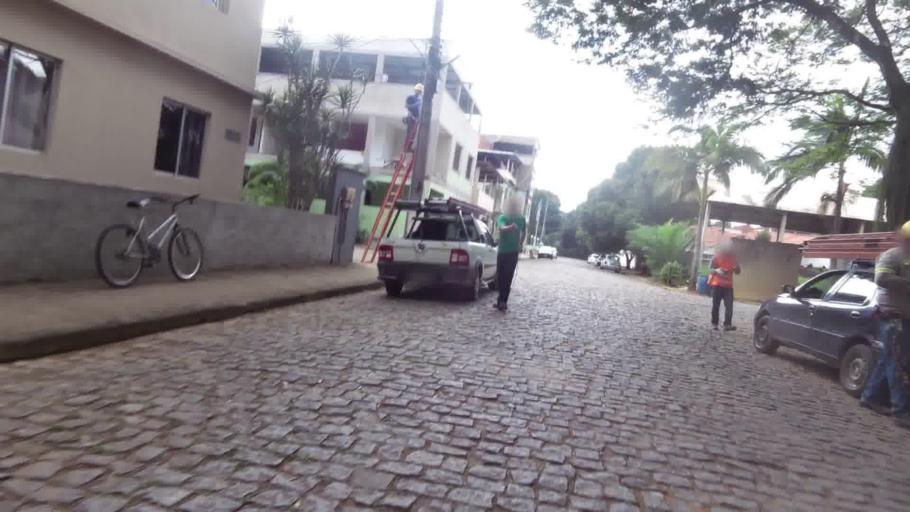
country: BR
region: Espirito Santo
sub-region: Alfredo Chaves
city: Alfredo Chaves
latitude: -20.6352
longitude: -40.7473
